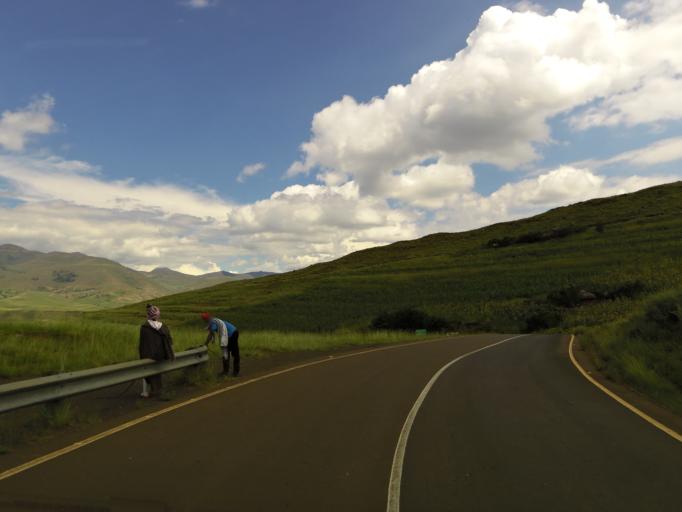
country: LS
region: Thaba-Tseka
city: Thaba-Tseka
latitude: -29.1556
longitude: 28.4808
